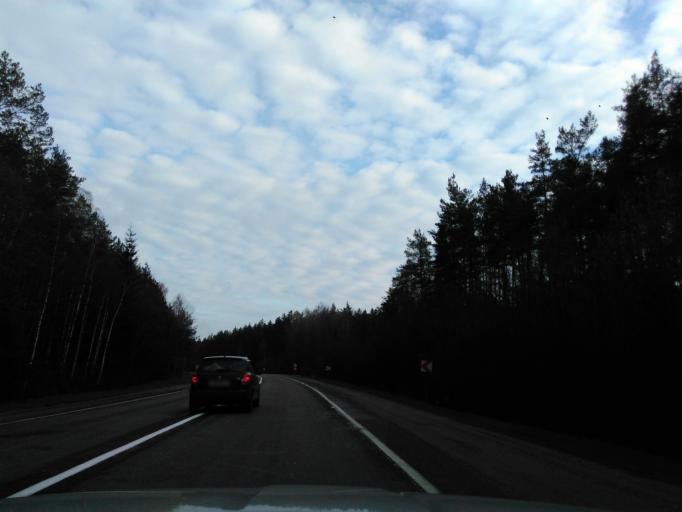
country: BY
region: Minsk
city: Plyeshchanitsy
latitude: 54.3843
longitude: 27.8733
